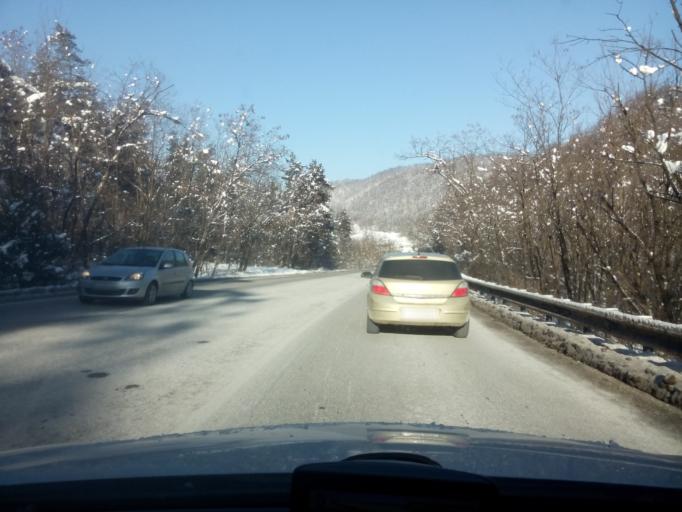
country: RO
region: Valcea
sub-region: Comuna Milcoiu
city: Milcoiu
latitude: 45.0541
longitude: 24.4511
